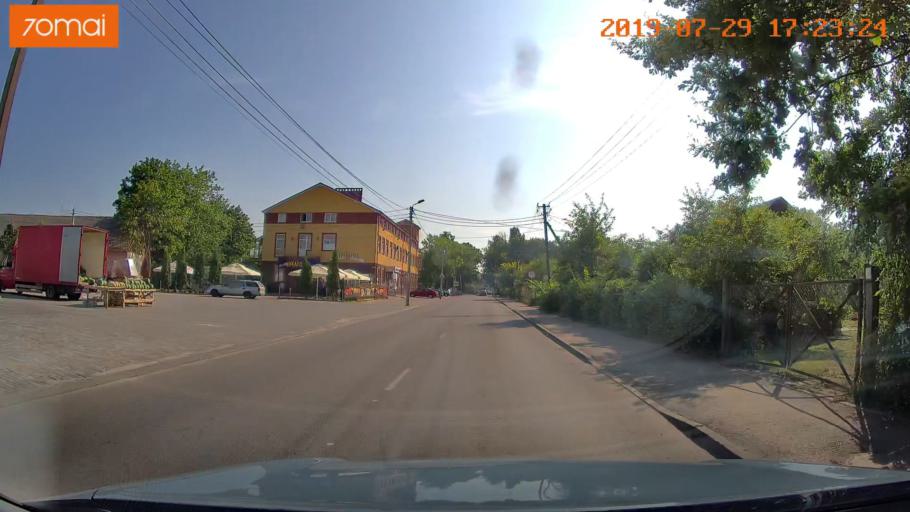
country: RU
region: Kaliningrad
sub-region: Gorod Kaliningrad
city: Kaliningrad
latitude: 54.7660
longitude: 20.4454
